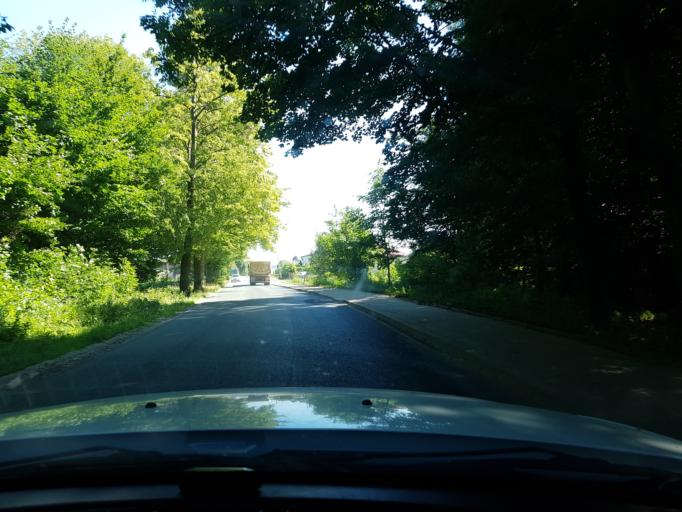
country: PL
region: West Pomeranian Voivodeship
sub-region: Powiat koszalinski
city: Mielno
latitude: 54.1986
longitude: 16.0538
